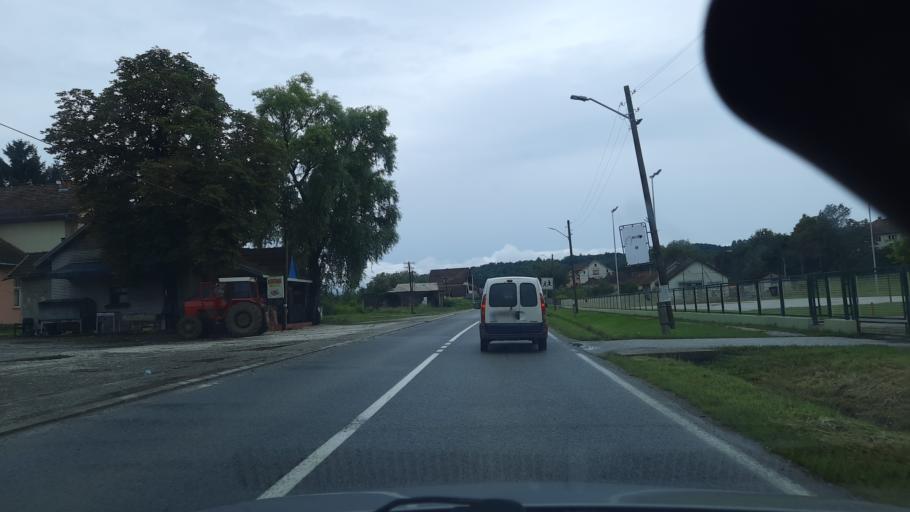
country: RS
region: Central Serbia
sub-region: Raski Okrug
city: Kraljevo
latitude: 43.7277
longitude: 20.8014
